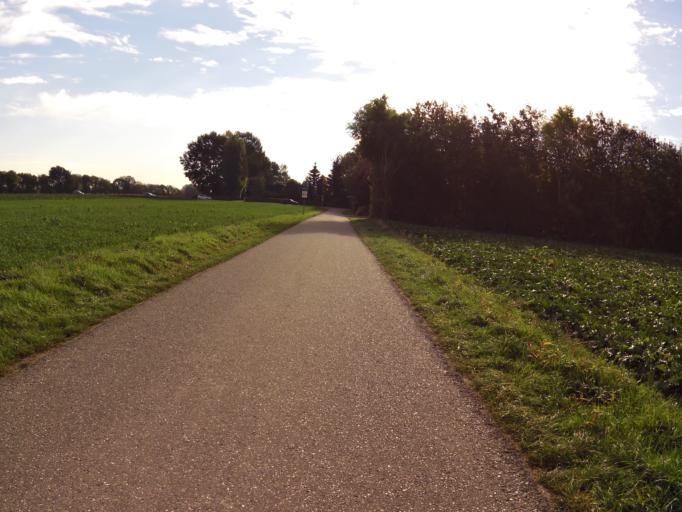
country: NL
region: Limburg
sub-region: Gemeente Schinnen
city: Doenrade
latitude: 50.9607
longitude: 5.8940
